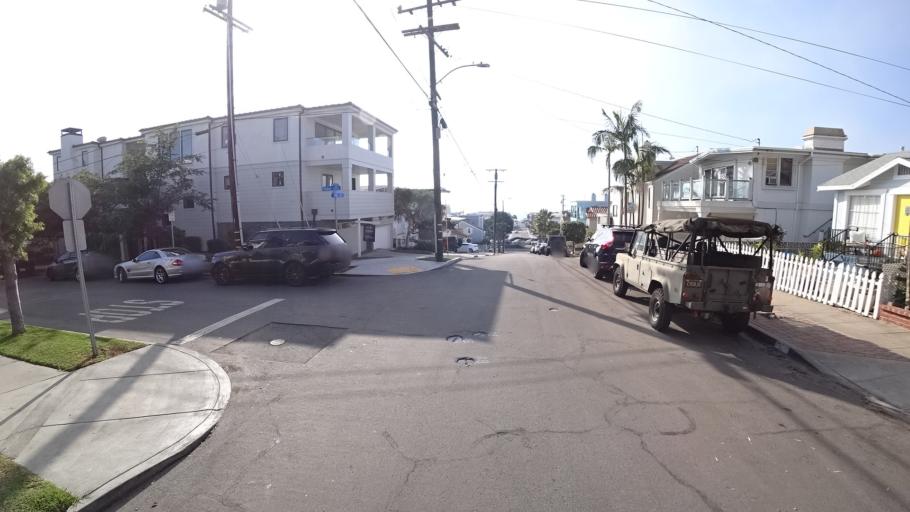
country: US
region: California
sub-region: Los Angeles County
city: Manhattan Beach
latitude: 33.8875
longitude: -118.4073
